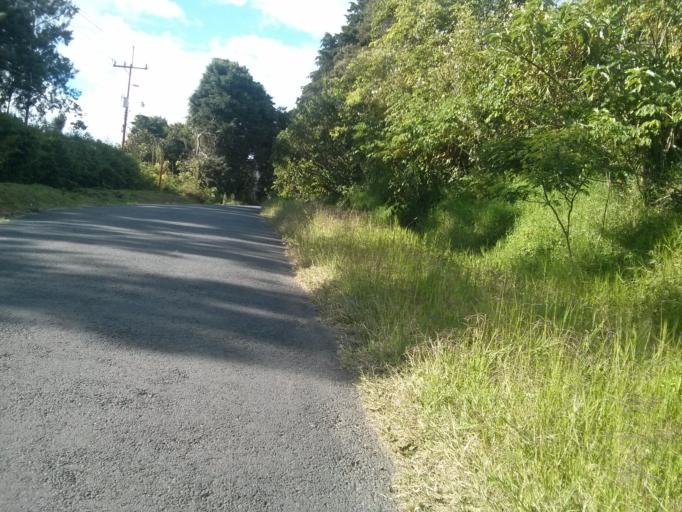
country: CR
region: Cartago
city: Tres Rios
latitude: 9.9113
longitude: -83.9493
